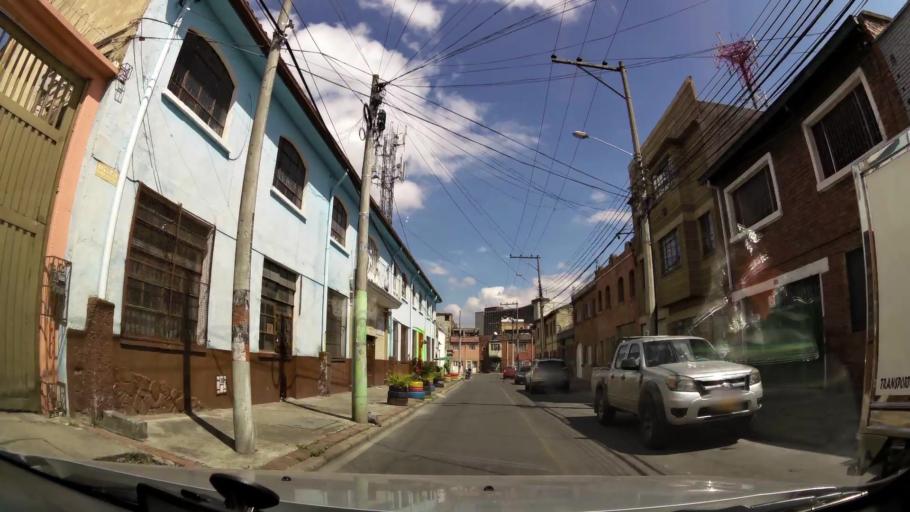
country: CO
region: Bogota D.C.
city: Bogota
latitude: 4.6216
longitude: -74.0797
